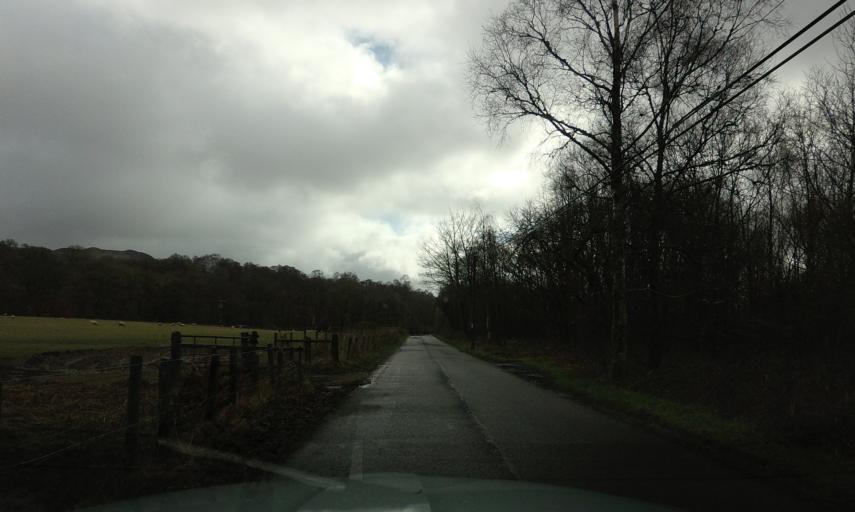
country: GB
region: Scotland
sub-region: West Dunbartonshire
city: Balloch
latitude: 56.1032
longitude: -4.5655
